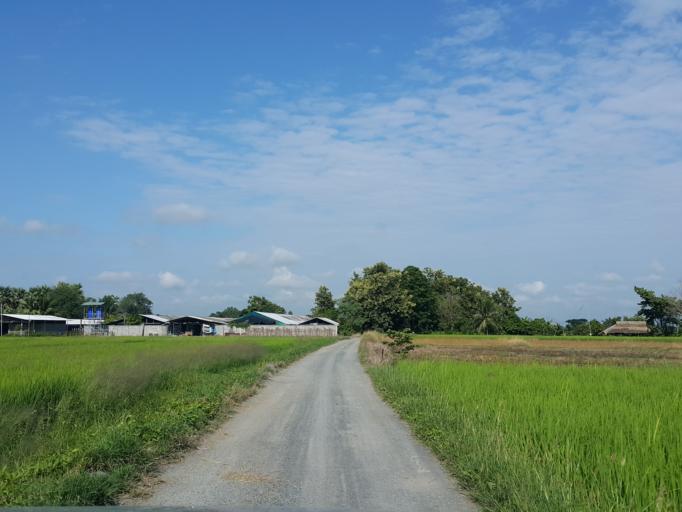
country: TH
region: Chiang Mai
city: San Kamphaeng
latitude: 18.8253
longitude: 99.1636
